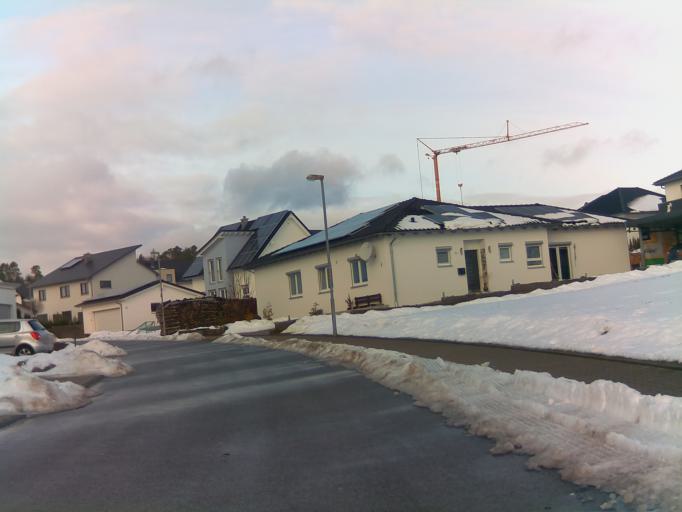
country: DE
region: Baden-Wuerttemberg
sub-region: Karlsruhe Region
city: Mudau
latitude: 49.5396
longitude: 9.1979
